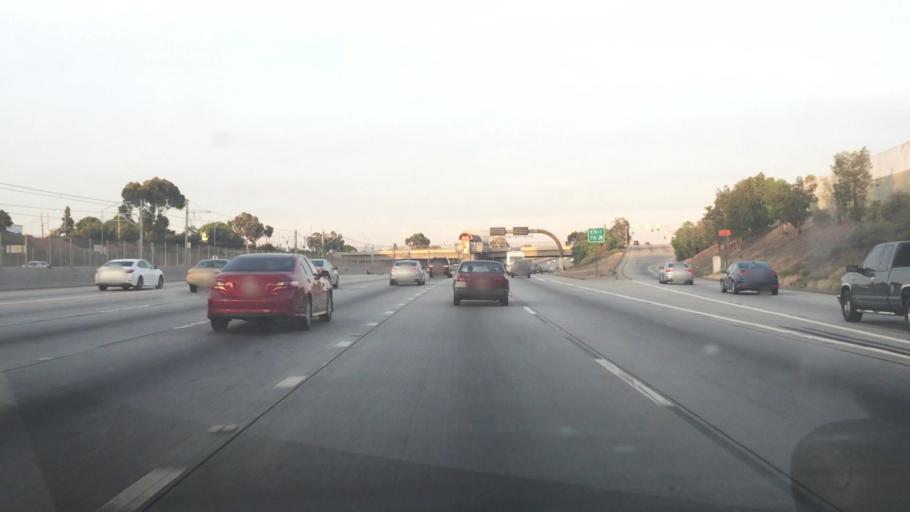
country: US
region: California
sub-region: Los Angeles County
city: West Athens
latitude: 33.9282
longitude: -118.2958
